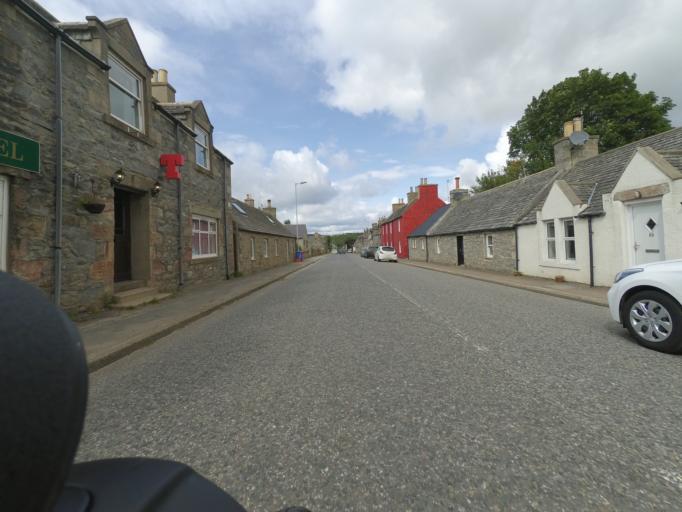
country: GB
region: Scotland
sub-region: Highland
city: Grantown on Spey
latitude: 57.2523
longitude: -3.3802
